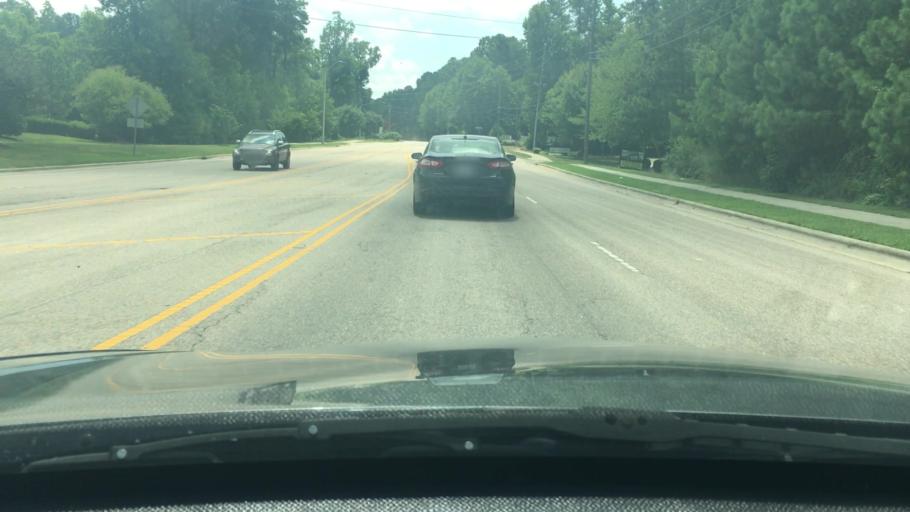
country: US
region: North Carolina
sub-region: Wake County
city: Cary
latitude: 35.7972
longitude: -78.7943
